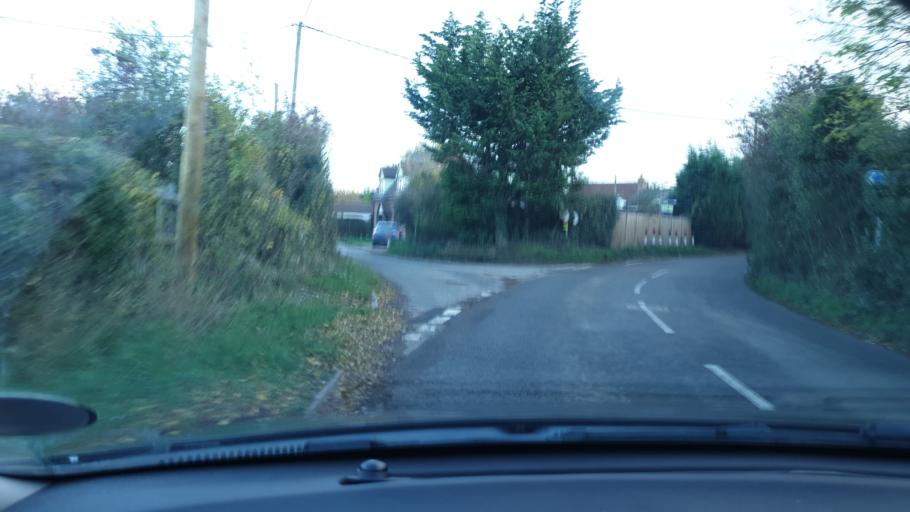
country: GB
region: England
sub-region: Essex
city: Little Clacton
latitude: 51.8967
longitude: 1.1467
